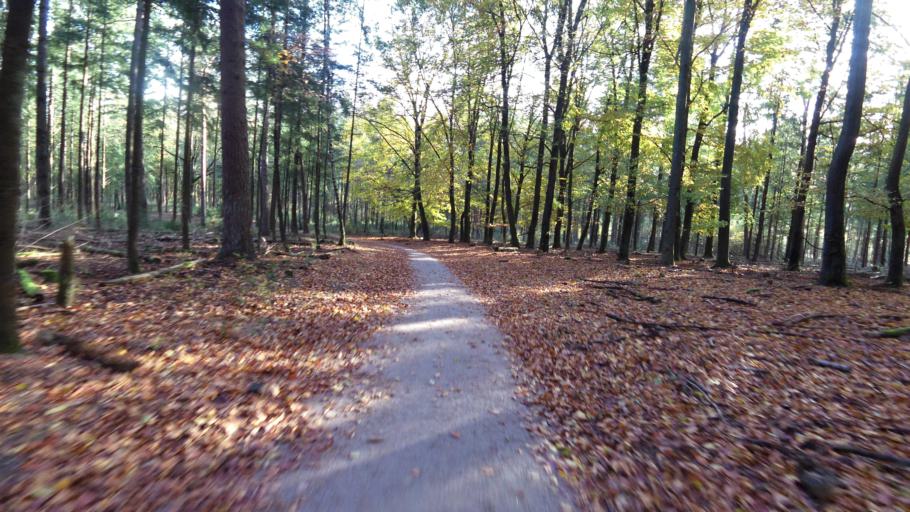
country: NL
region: Gelderland
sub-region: Gemeente Epe
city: Epe
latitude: 52.3832
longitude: 5.9517
